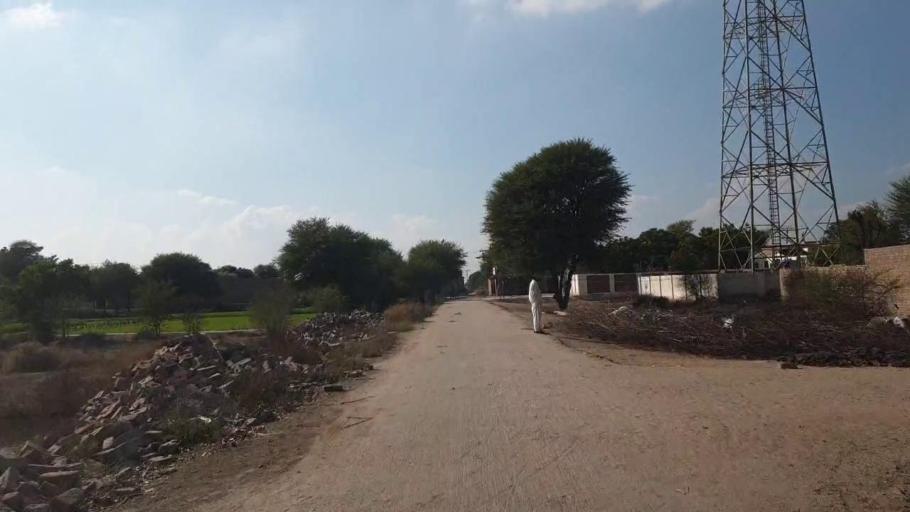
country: PK
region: Sindh
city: Shahpur Chakar
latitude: 26.1023
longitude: 68.5676
